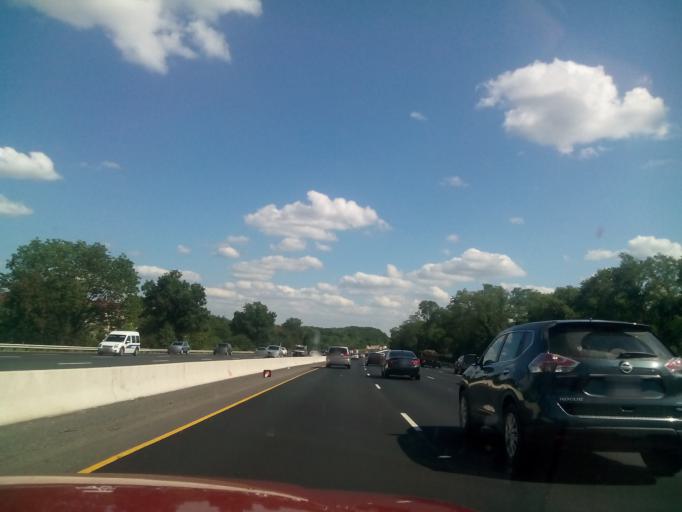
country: US
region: New Jersey
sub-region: Morris County
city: Rockaway
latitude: 40.9085
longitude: -74.5021
